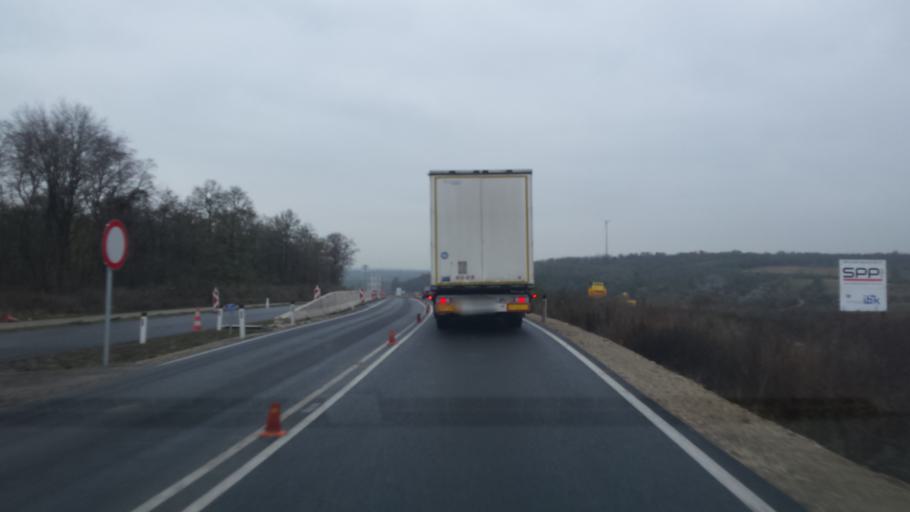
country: AT
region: Lower Austria
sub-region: Politischer Bezirk Mistelbach
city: Wilfersdorf
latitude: 48.5243
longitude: 16.6262
